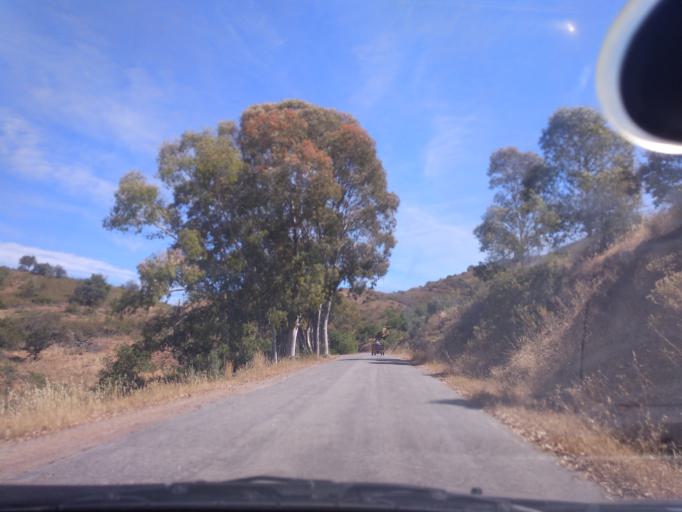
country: PT
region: Faro
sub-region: Olhao
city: Moncarapacho
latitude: 37.1605
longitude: -7.7987
